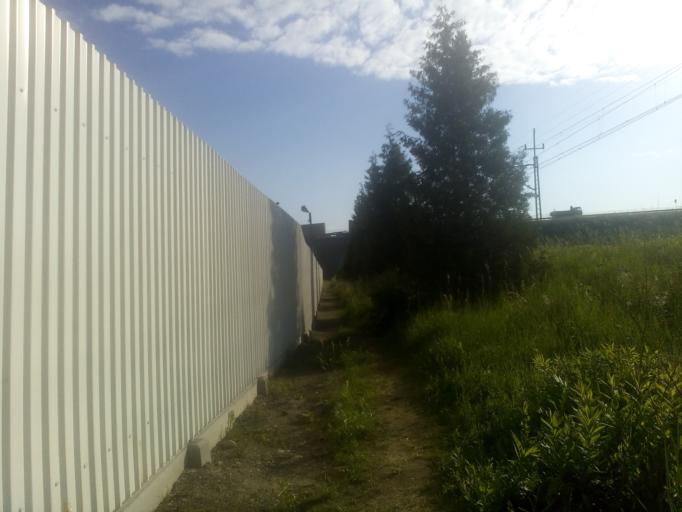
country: PL
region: Lesser Poland Voivodeship
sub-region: Powiat nowosadecki
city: Stary Sacz
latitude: 49.5720
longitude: 20.6465
